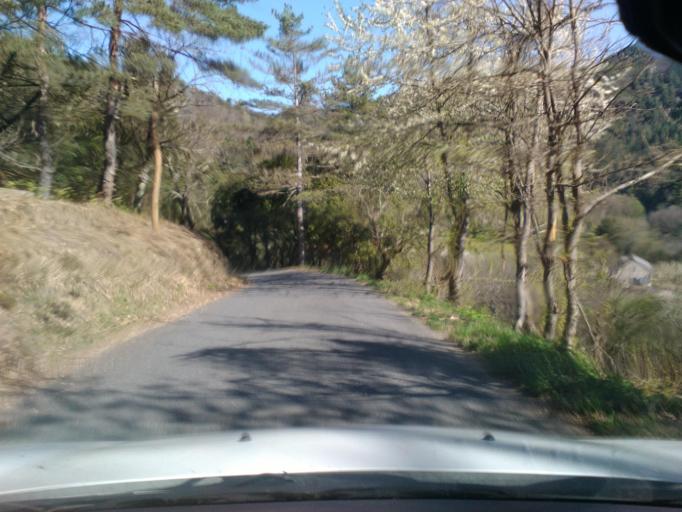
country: FR
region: Languedoc-Roussillon
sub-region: Departement du Gard
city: Saint-Jean-du-Gard
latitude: 44.1640
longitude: 3.7637
